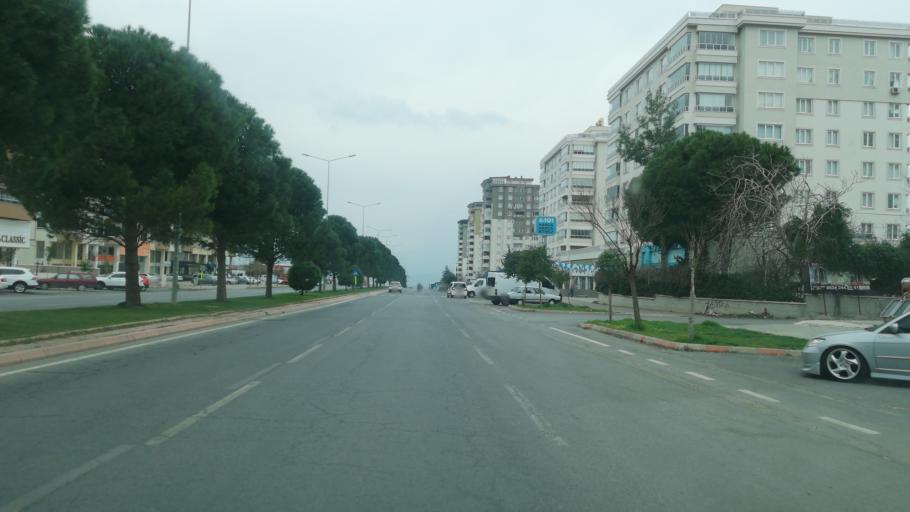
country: TR
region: Kahramanmaras
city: Kahramanmaras
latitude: 37.6001
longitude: 36.8288
